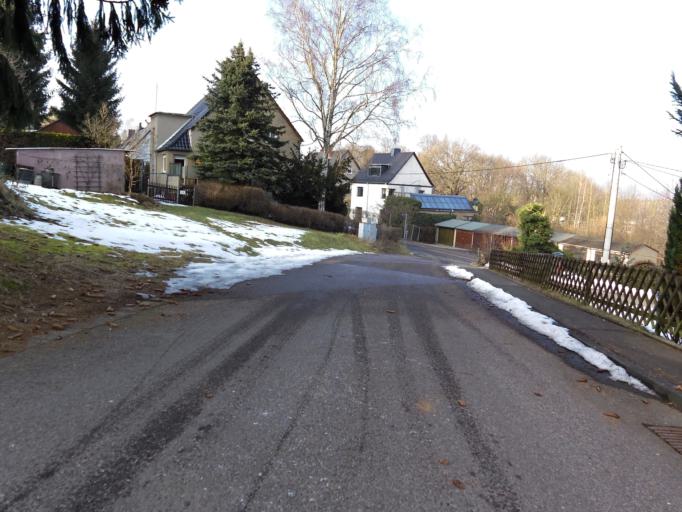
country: DE
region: Saxony
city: Glauchau
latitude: 50.8214
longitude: 12.5603
